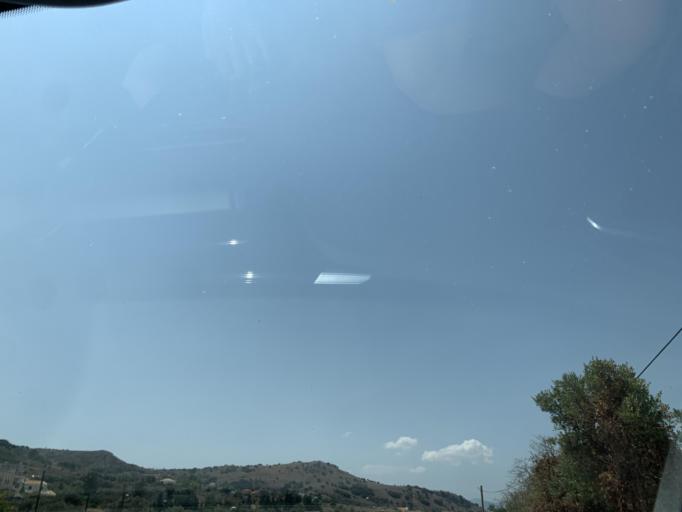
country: GR
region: Crete
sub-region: Nomos Chanias
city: Kalivai
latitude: 35.4491
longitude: 24.2230
